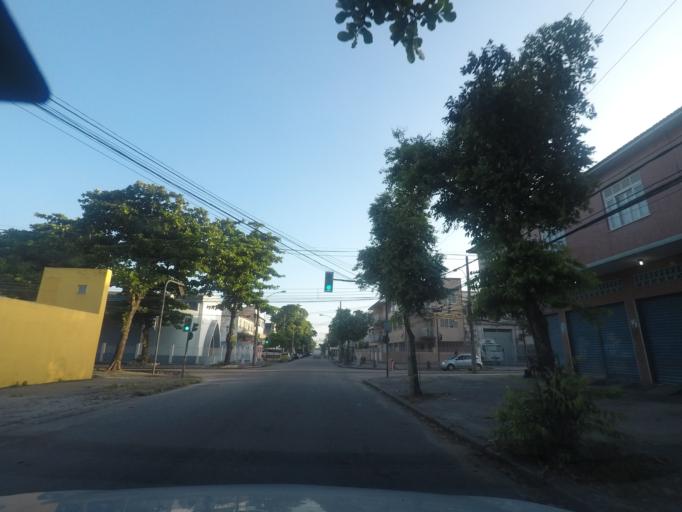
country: BR
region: Rio de Janeiro
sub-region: Duque De Caxias
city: Duque de Caxias
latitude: -22.8324
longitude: -43.2748
